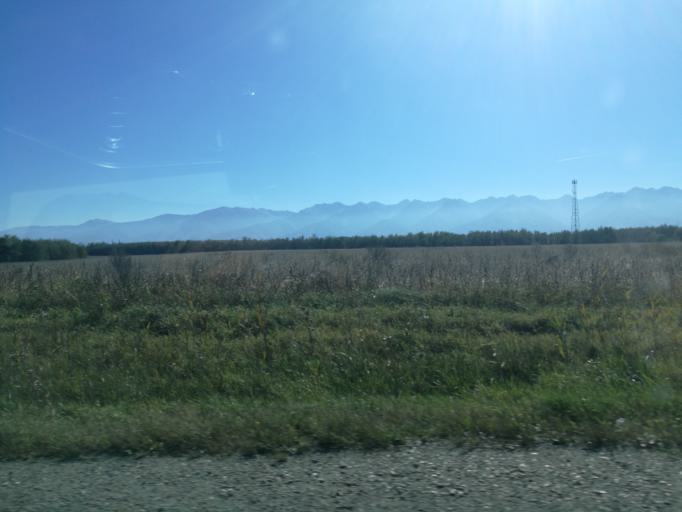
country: RO
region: Brasov
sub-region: Comuna Vistea de Jos
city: Vistea de Jos
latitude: 45.7920
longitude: 24.6985
